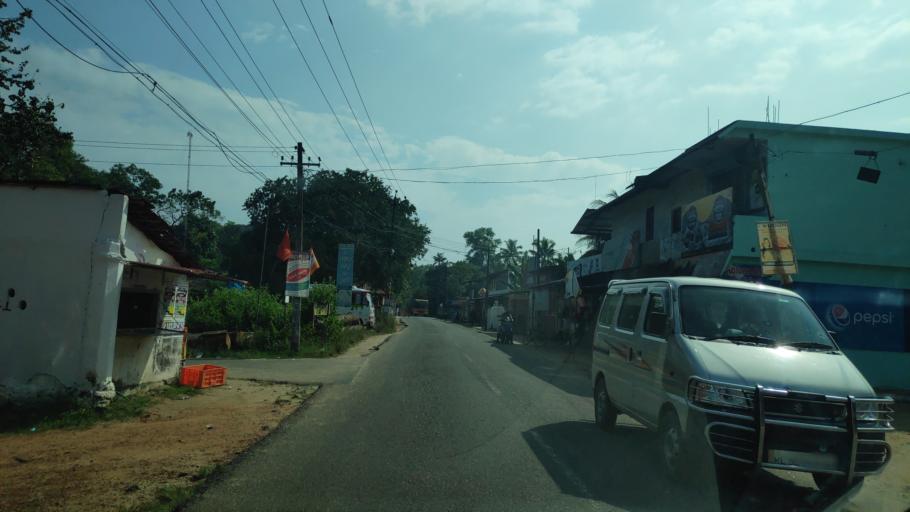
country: IN
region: Kerala
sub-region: Alappuzha
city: Alleppey
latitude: 9.5643
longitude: 76.3092
